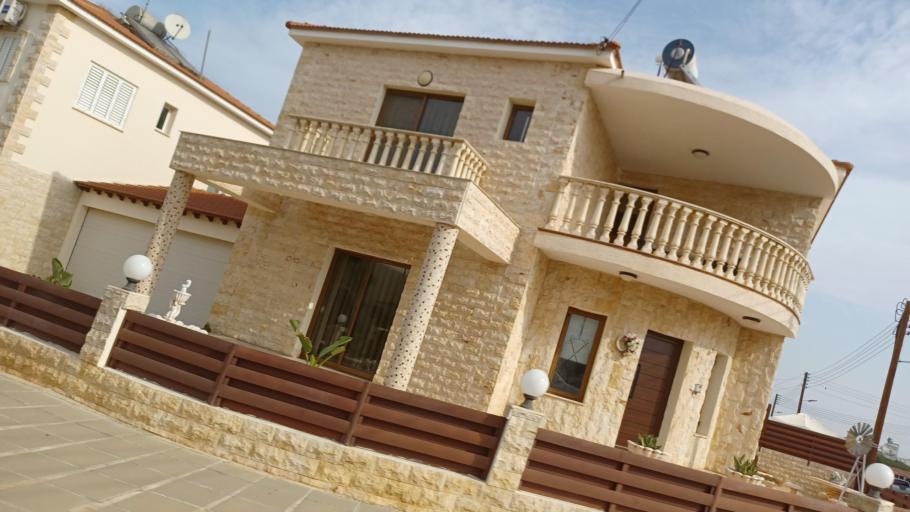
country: CY
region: Ammochostos
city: Frenaros
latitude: 35.0483
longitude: 33.9266
